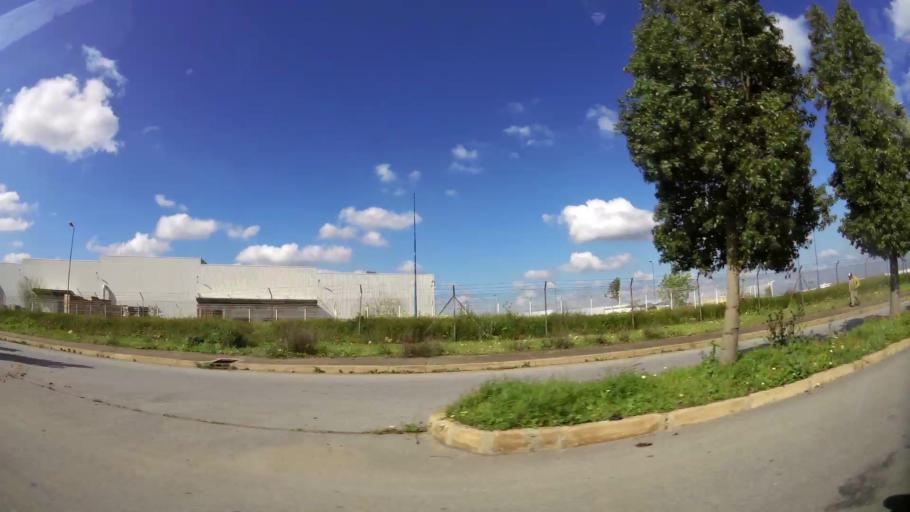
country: MA
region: Grand Casablanca
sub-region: Mediouna
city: Mediouna
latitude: 33.3911
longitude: -7.5449
